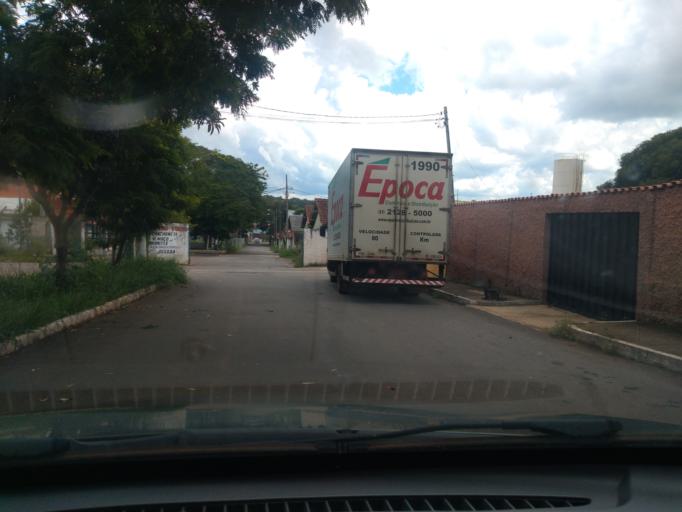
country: BR
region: Minas Gerais
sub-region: Tres Coracoes
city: Tres Coracoes
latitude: -21.6720
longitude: -45.2709
